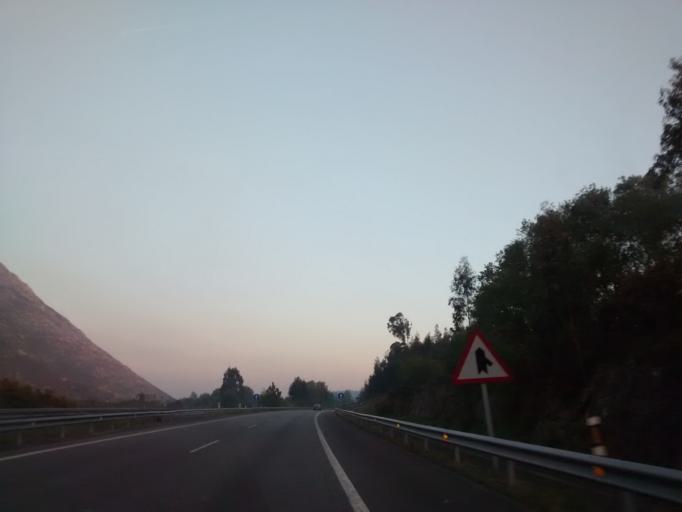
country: ES
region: Asturias
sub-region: Province of Asturias
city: Ribadesella
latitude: 43.4371
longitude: -5.0143
